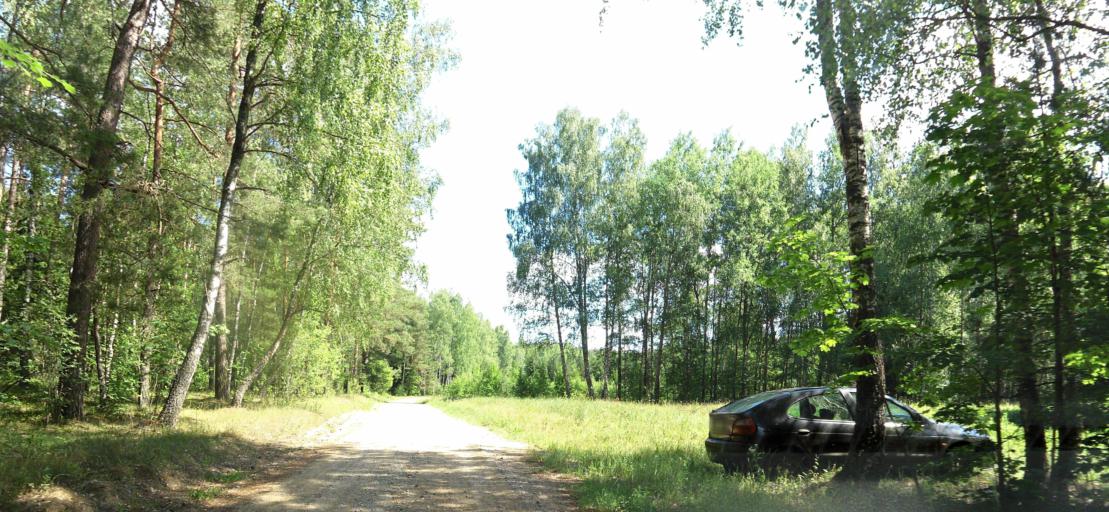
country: LT
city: Nemencine
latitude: 54.8259
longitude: 25.4141
